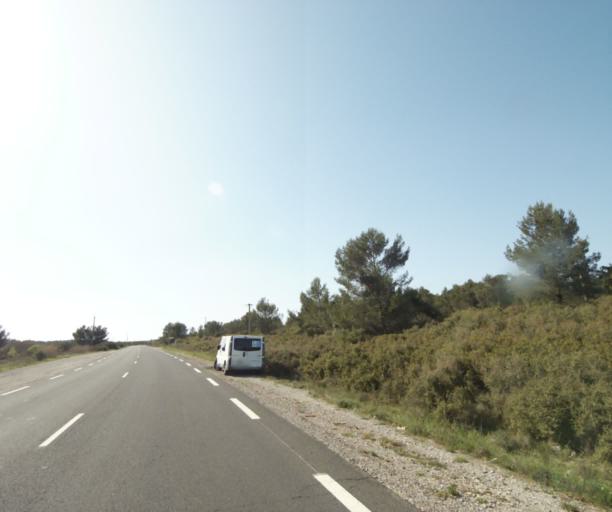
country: FR
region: Languedoc-Roussillon
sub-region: Departement de l'Herault
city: Grabels
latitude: 43.6303
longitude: 3.7722
